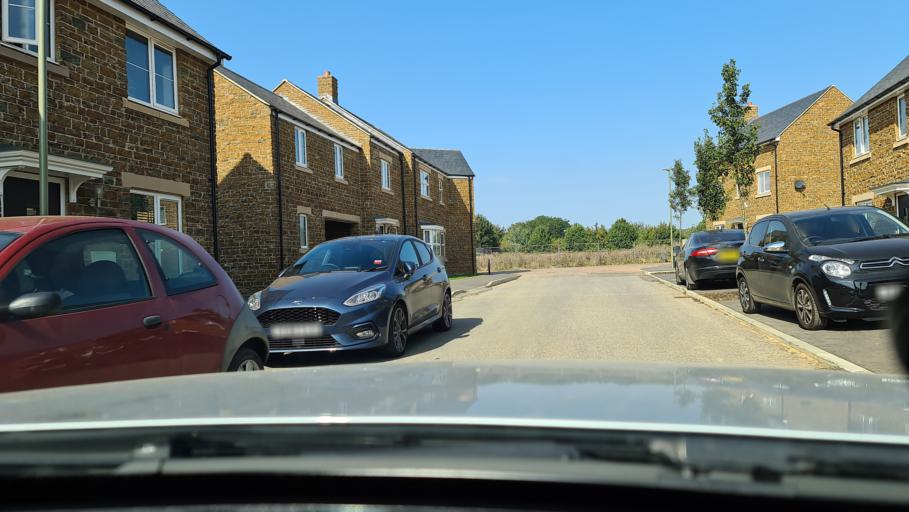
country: GB
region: England
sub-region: Oxfordshire
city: Hanwell
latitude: 52.0782
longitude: -1.3689
